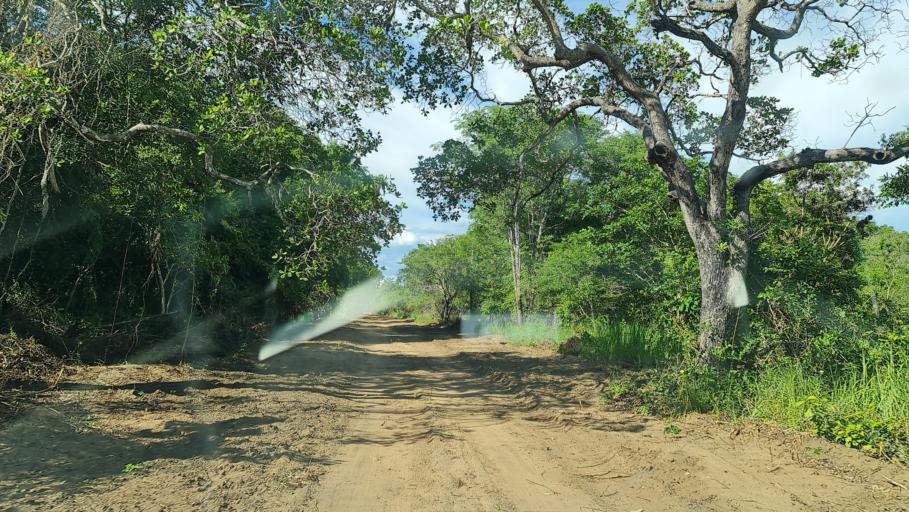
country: MZ
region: Nampula
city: Antonio Enes
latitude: -15.5218
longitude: 40.1281
